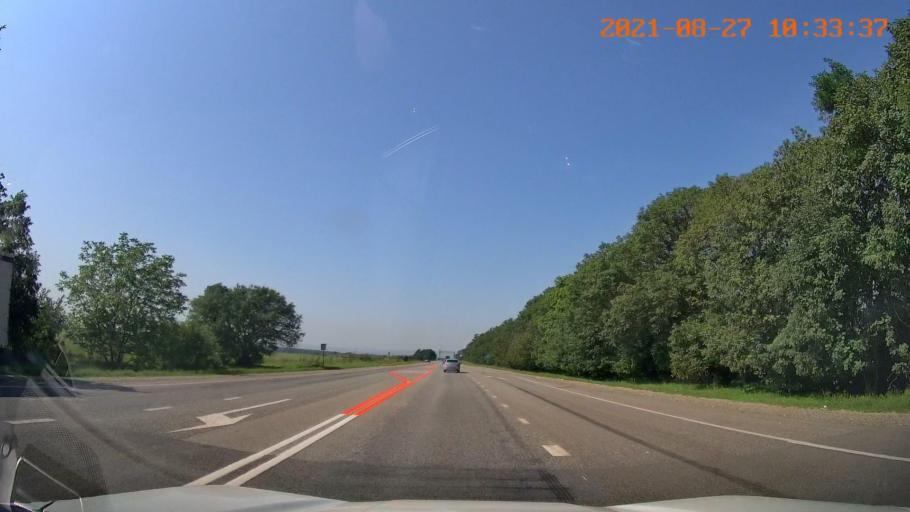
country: RU
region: Karachayevo-Cherkesiya
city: Cherkessk
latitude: 44.2590
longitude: 42.1185
